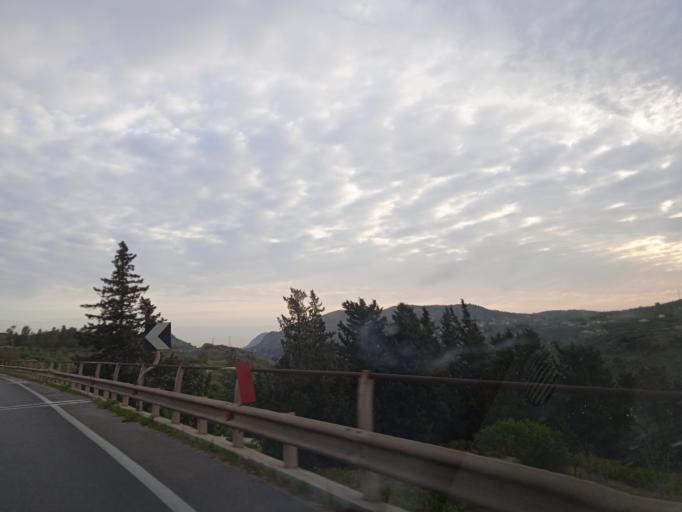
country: IT
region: Sicily
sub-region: Palermo
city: Portella di Mare
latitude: 38.0503
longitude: 13.4615
